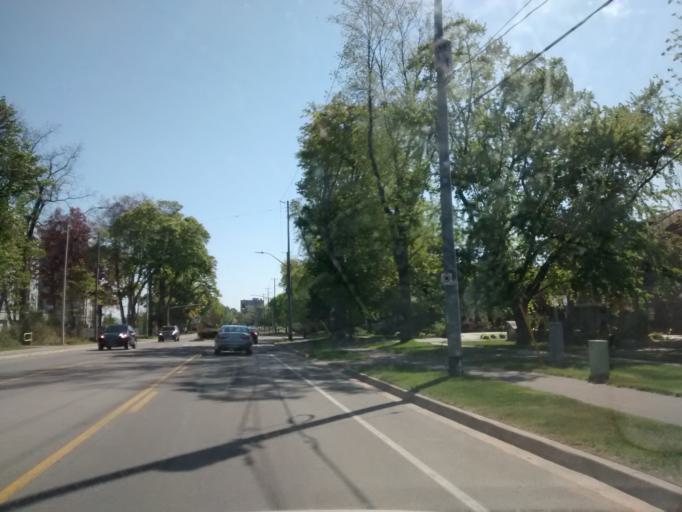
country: CA
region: Ontario
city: Oakville
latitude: 43.3750
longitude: -79.7206
